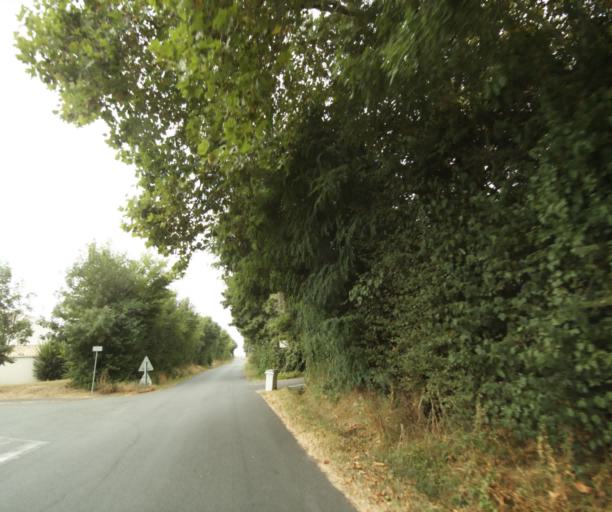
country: FR
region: Poitou-Charentes
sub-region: Departement de la Charente-Maritime
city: Tonnay-Charente
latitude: 45.9511
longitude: -0.8743
